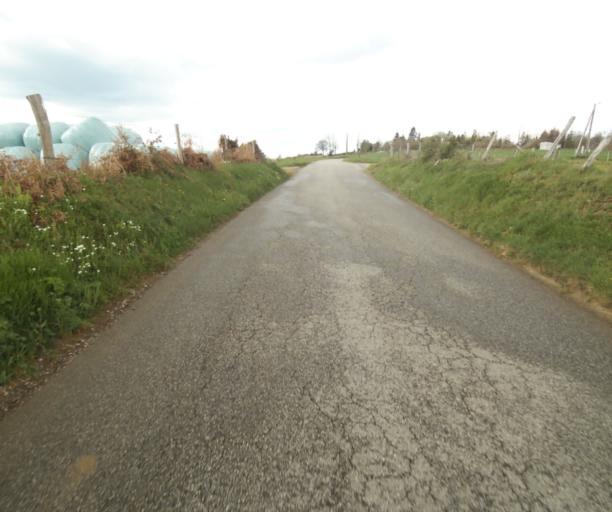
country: FR
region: Limousin
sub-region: Departement de la Correze
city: Tulle
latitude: 45.2803
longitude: 1.7475
